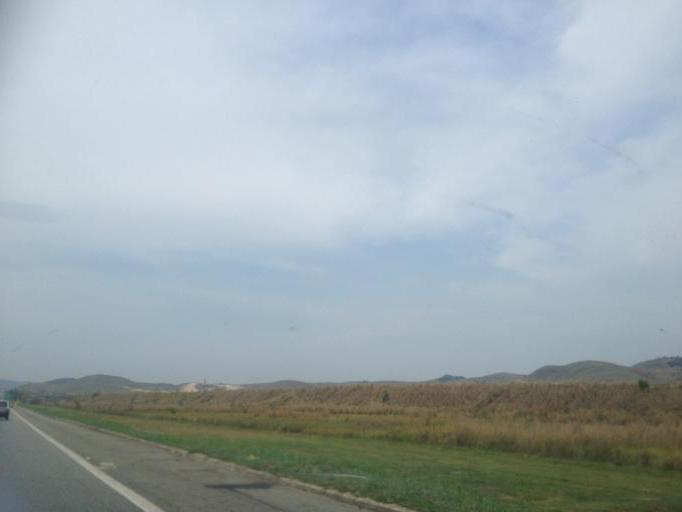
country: BR
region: Rio de Janeiro
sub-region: Porto Real
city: Porto Real
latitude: -22.4515
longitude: -44.3465
